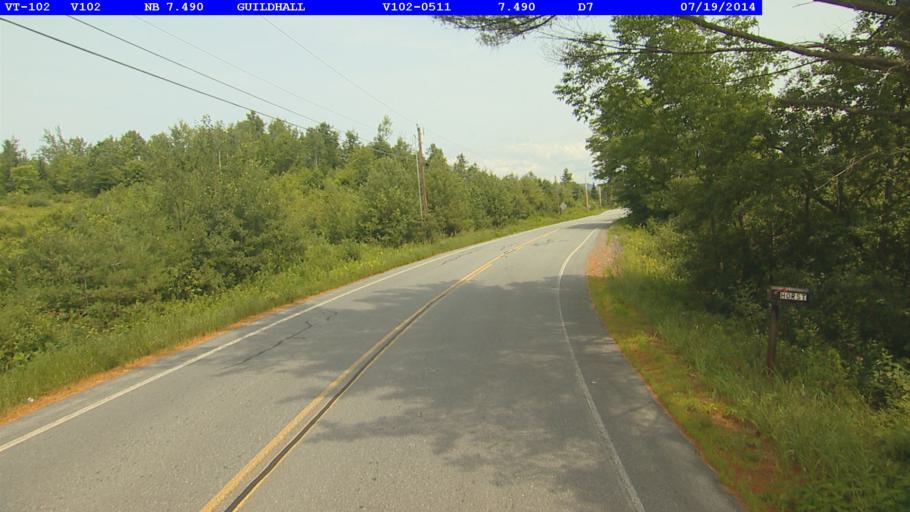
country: US
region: Vermont
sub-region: Essex County
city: Guildhall
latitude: 44.5679
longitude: -71.5603
